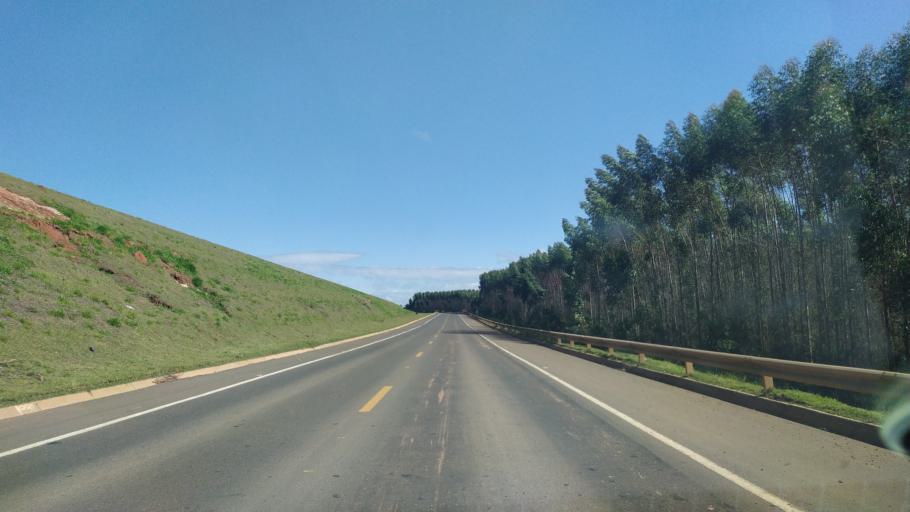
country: BR
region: Parana
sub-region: Telemaco Borba
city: Telemaco Borba
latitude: -24.2421
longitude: -50.7693
